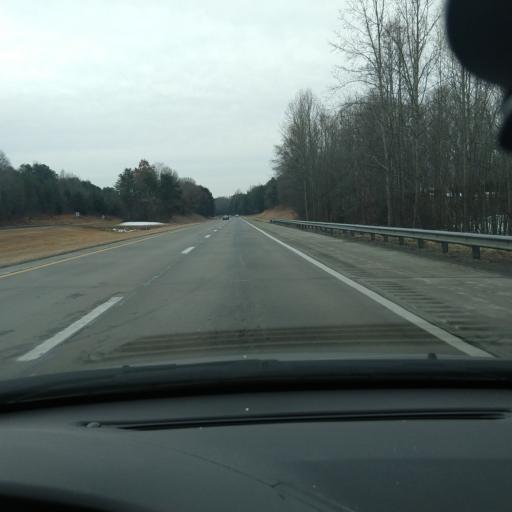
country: US
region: North Carolina
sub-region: Davidson County
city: Midway
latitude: 35.9993
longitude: -80.2378
